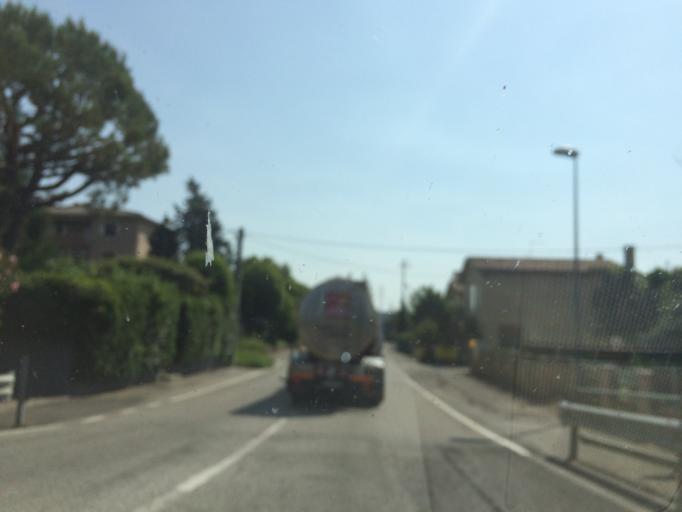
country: IT
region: Veneto
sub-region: Provincia di Padova
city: Cittadella
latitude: 45.6391
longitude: 11.7751
